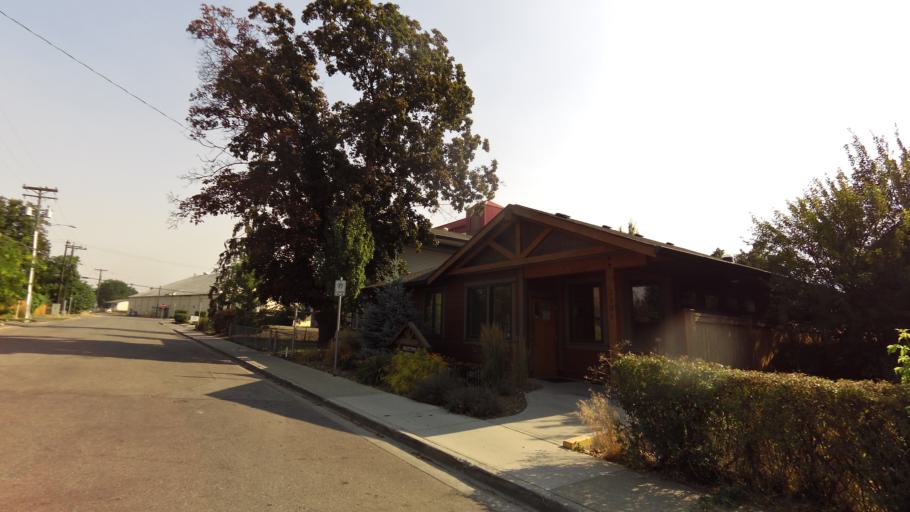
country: CA
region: British Columbia
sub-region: Regional District of North Okanagan
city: Vernon
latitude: 50.2679
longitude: -119.2723
